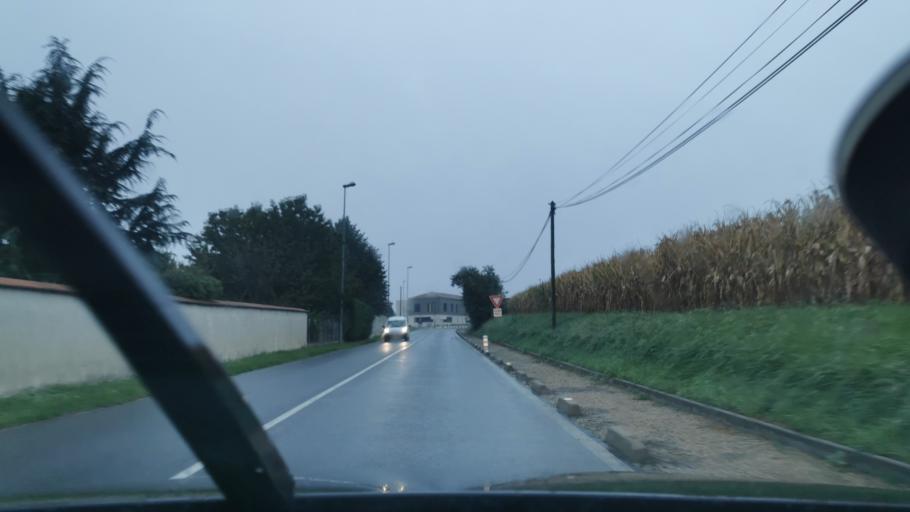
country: FR
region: Rhone-Alpes
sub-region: Departement de l'Ain
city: Civrieux
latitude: 45.9498
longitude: 4.8829
